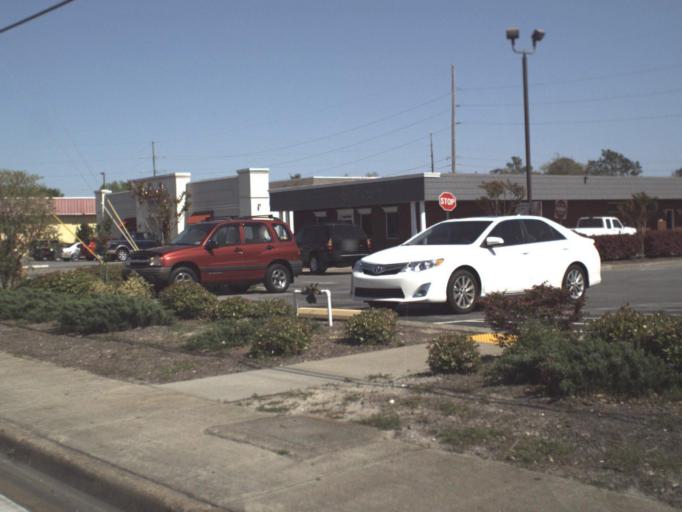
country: US
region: Florida
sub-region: Okaloosa County
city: Mary Esther
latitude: 30.4234
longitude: -86.6492
